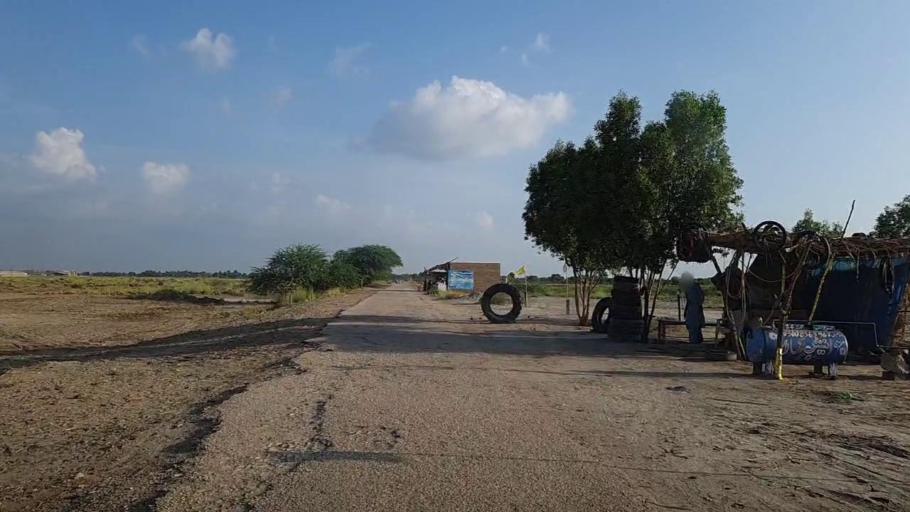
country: PK
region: Sindh
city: Hingorja
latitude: 27.0746
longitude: 68.4188
